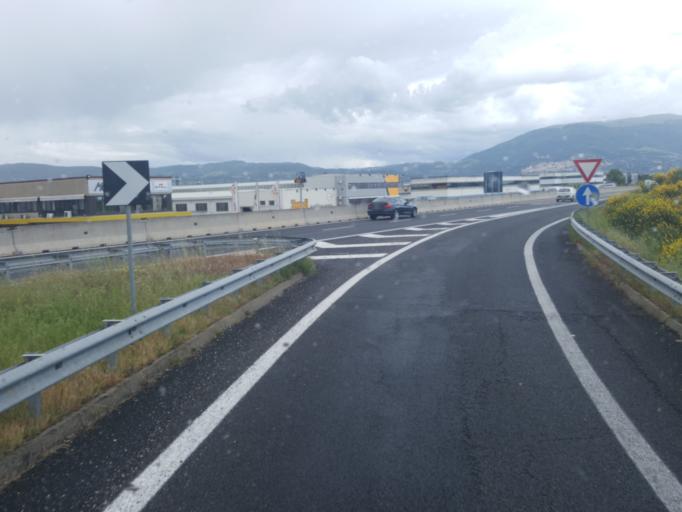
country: IT
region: Umbria
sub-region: Provincia di Perugia
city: Ospedalicchio
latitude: 43.0732
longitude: 12.5153
